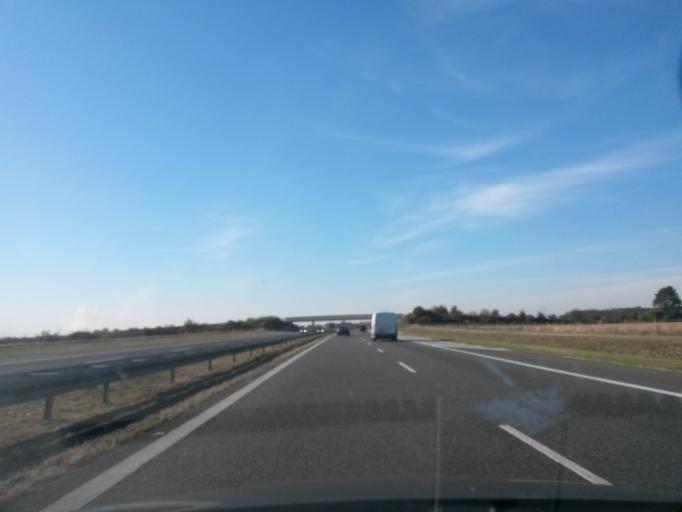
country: PL
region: Opole Voivodeship
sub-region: Powiat brzeski
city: Grodkow
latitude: 50.7760
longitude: 17.3612
